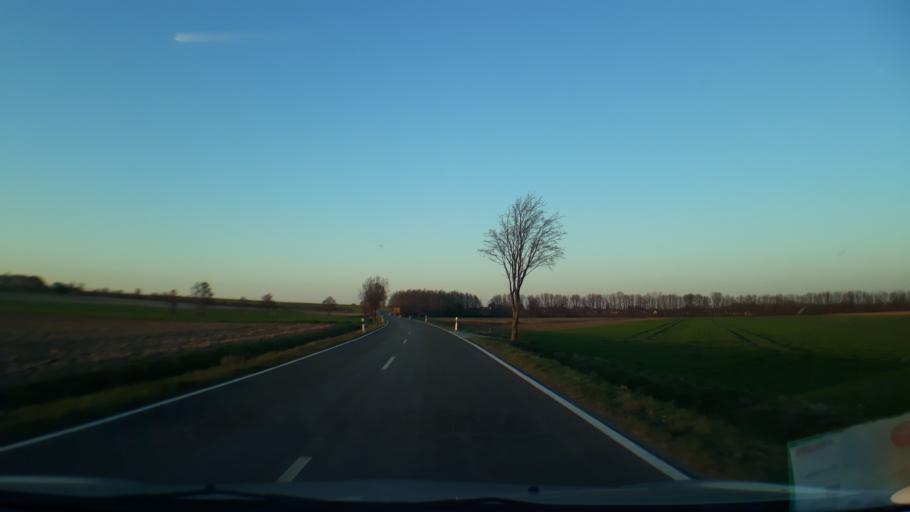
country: DE
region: North Rhine-Westphalia
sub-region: Regierungsbezirk Koln
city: Vettweiss
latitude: 50.6959
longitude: 6.6023
